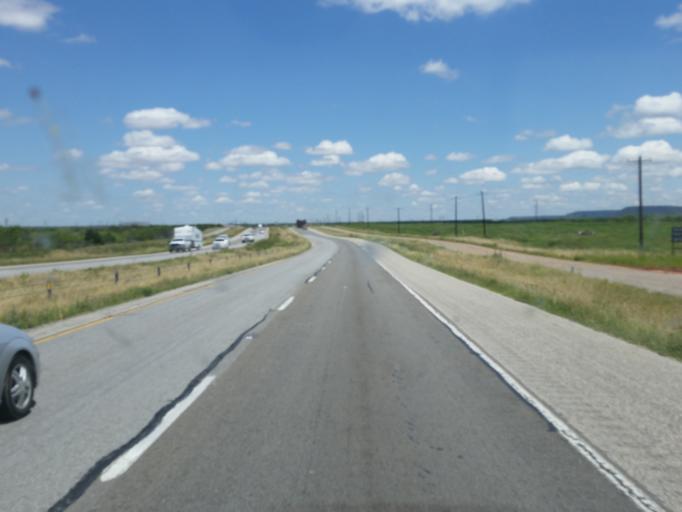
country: US
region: Texas
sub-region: Nolan County
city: Sweetwater
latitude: 32.4924
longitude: -100.2536
